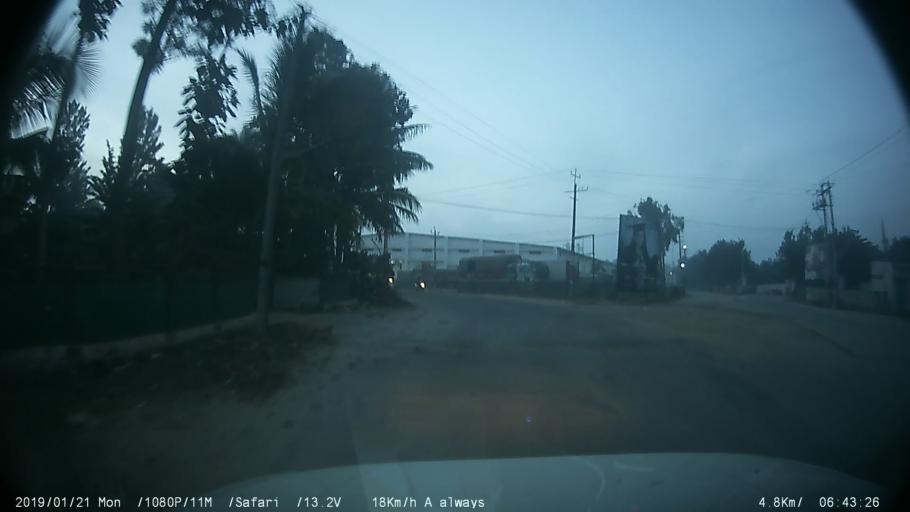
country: IN
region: Karnataka
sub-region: Bangalore Urban
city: Anekal
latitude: 12.8214
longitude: 77.6227
